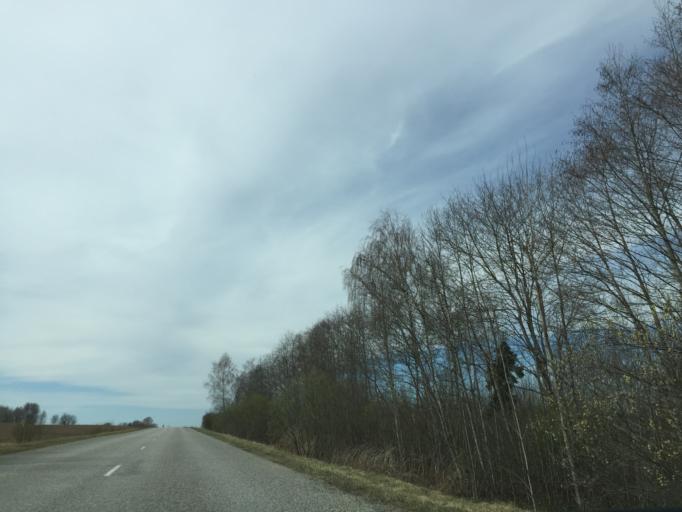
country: LV
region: Valkas Rajons
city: Valka
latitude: 57.7802
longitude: 25.9387
